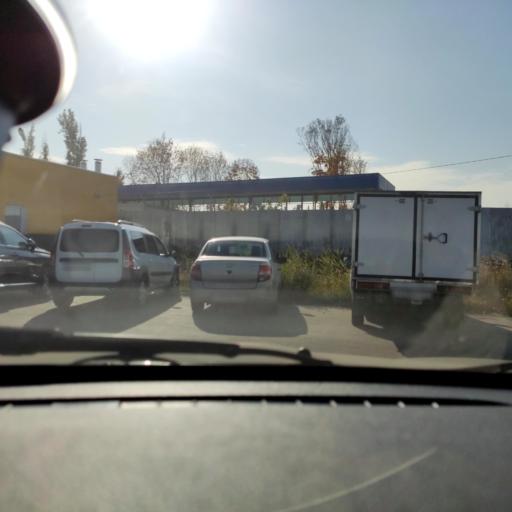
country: RU
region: Samara
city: Tol'yatti
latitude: 53.5481
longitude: 49.2847
